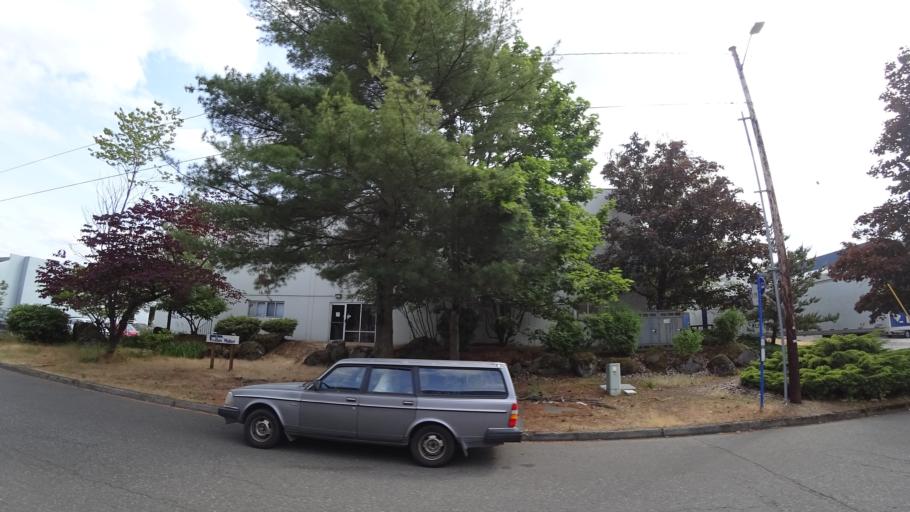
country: US
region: Washington
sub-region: Clark County
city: Vancouver
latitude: 45.5808
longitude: -122.6394
